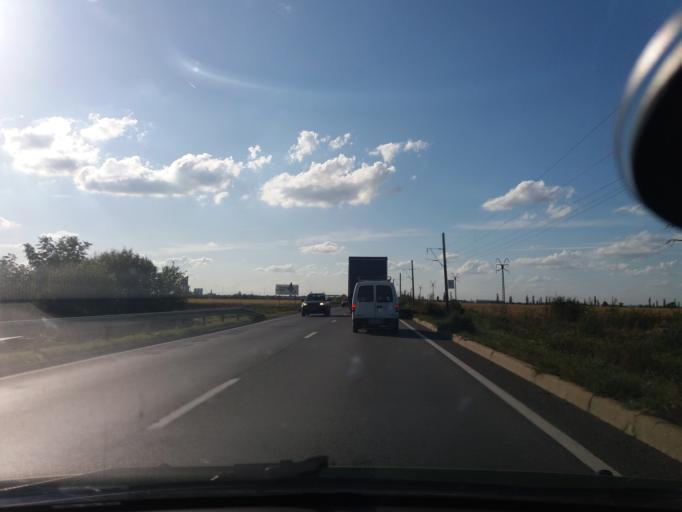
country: RO
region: Arad
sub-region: Comuna Vladimirescu
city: Mandruloc
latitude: 46.1539
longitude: 21.4411
